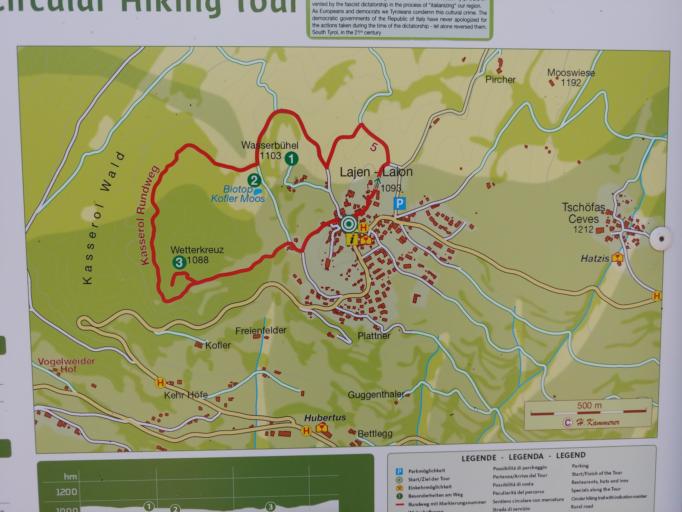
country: IT
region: Trentino-Alto Adige
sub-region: Bolzano
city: Laion
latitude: 46.6087
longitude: 11.5647
